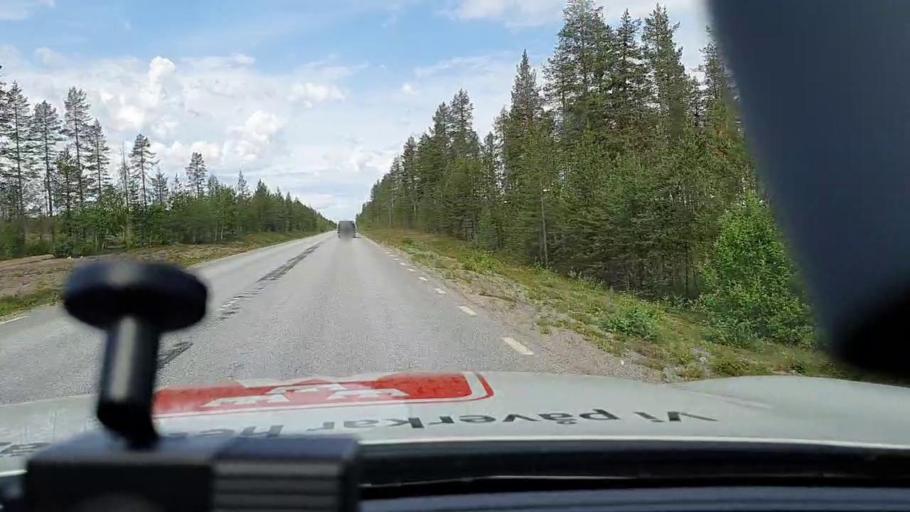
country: SE
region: Norrbotten
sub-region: Jokkmokks Kommun
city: Jokkmokk
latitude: 66.5202
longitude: 20.2157
